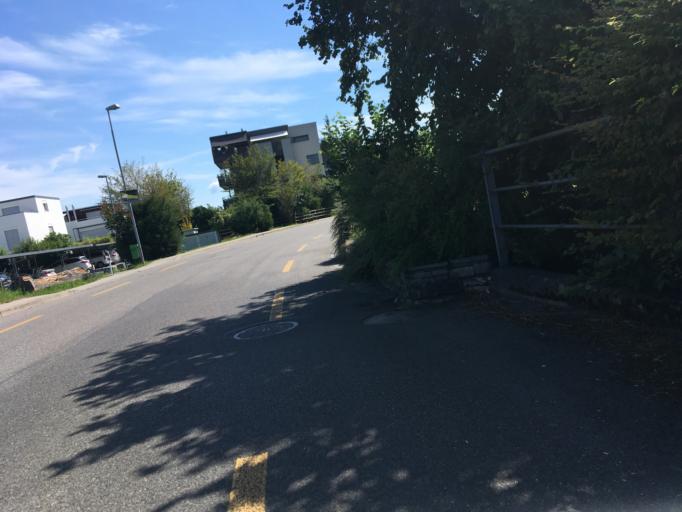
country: CH
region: Fribourg
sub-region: See District
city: Murten
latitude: 46.9384
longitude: 7.1307
